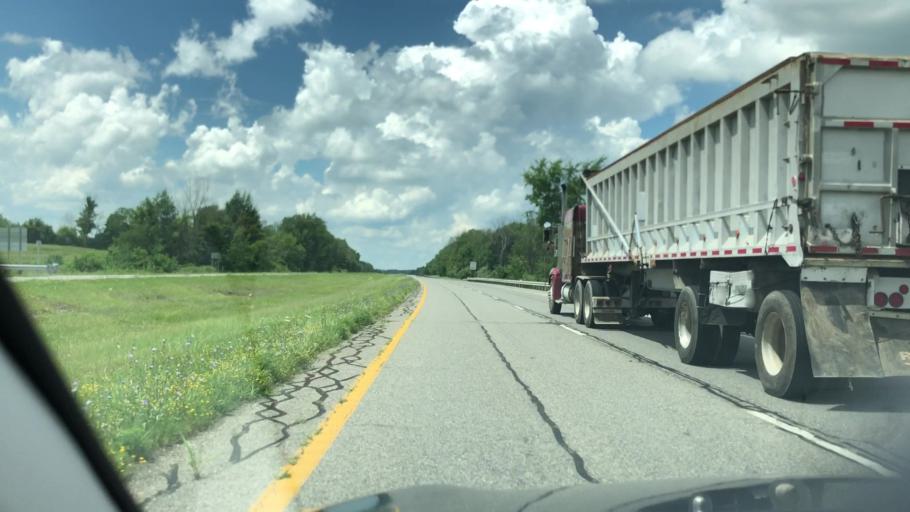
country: US
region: Ohio
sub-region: Stark County
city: Canal Fulton
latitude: 40.8925
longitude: -81.6254
